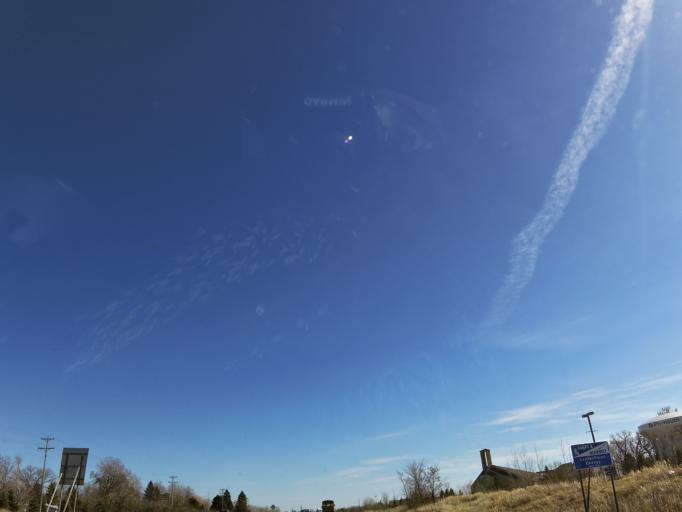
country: US
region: Minnesota
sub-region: Hennepin County
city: Plymouth
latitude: 45.0312
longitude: -93.5065
